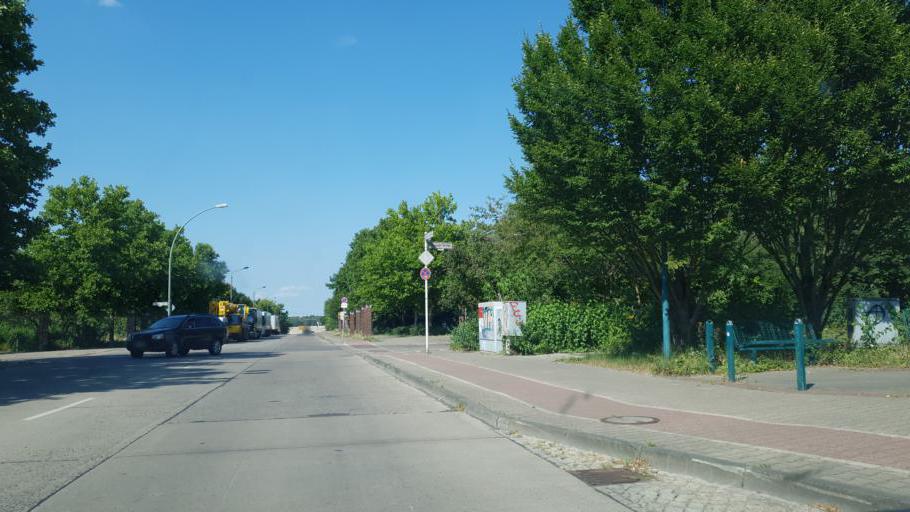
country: DE
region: Berlin
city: Hellersdorf
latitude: 52.5418
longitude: 13.6195
